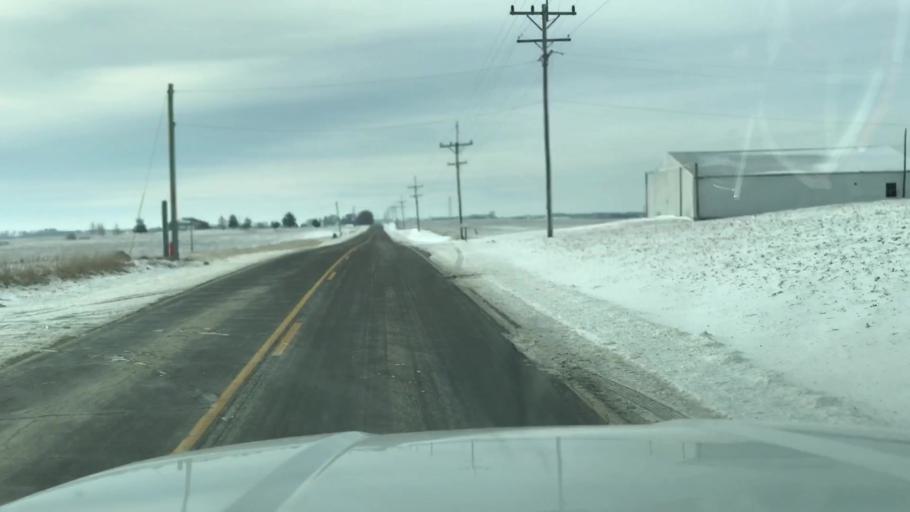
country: US
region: Missouri
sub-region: Holt County
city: Oregon
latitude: 40.0598
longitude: -95.1356
